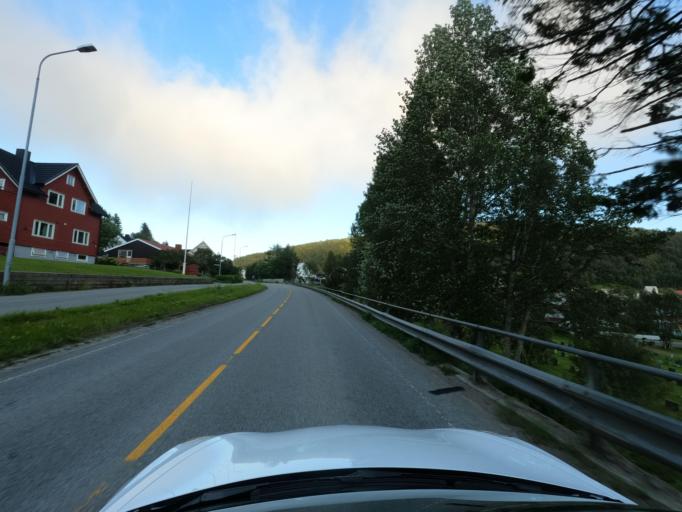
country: NO
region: Troms
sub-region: Harstad
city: Harstad
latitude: 68.8064
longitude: 16.5117
